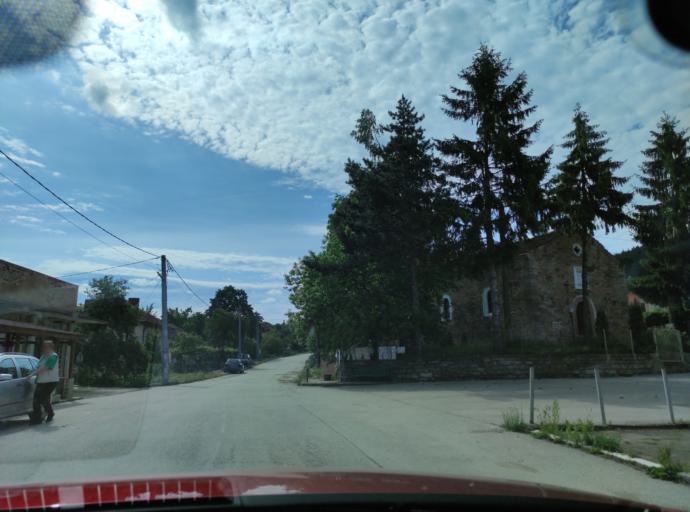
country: BG
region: Vidin
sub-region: Obshtina Belogradchik
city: Belogradchik
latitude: 43.5166
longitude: 22.7337
